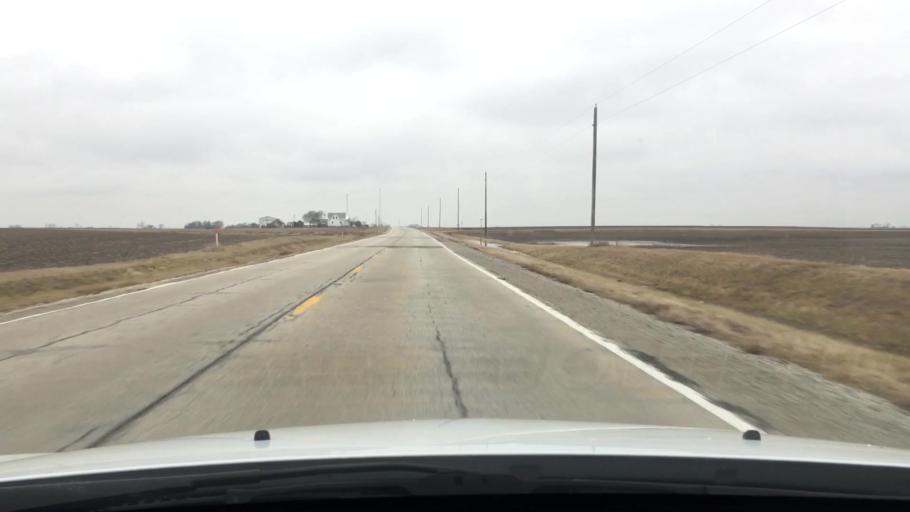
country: US
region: Illinois
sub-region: Iroquois County
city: Clifton
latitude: 40.8838
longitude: -87.9788
